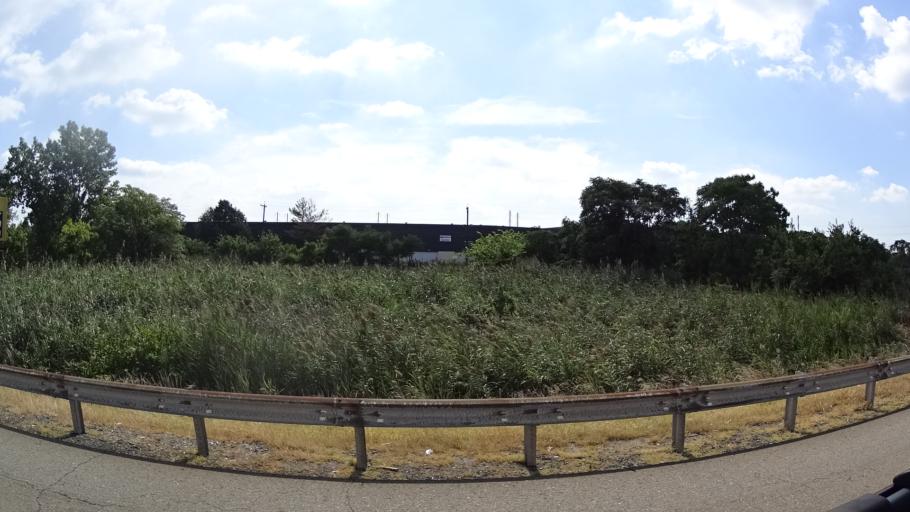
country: US
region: New Jersey
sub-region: Hudson County
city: Secaucus
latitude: 40.7703
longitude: -74.0626
